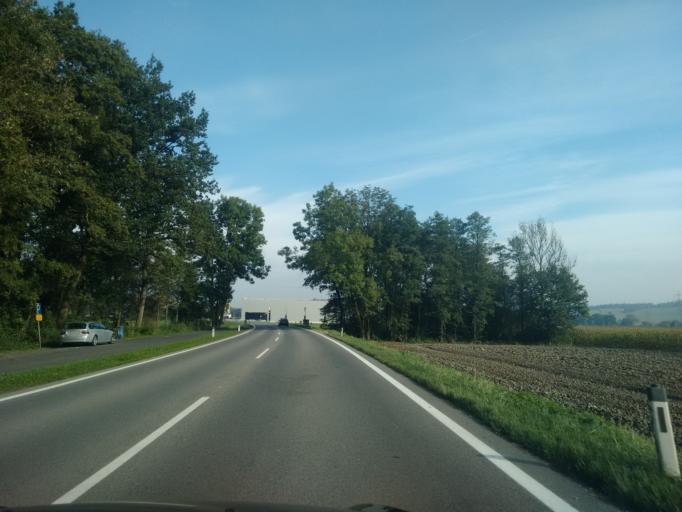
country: AT
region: Upper Austria
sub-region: Politischer Bezirk Grieskirchen
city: Grieskirchen
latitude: 48.2374
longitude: 13.7692
